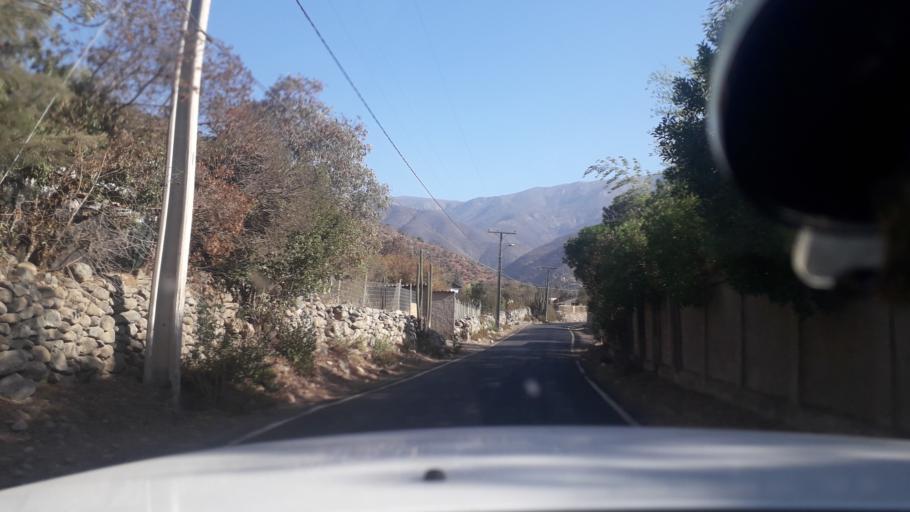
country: CL
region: Valparaiso
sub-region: Provincia de Marga Marga
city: Limache
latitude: -33.0545
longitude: -71.1118
